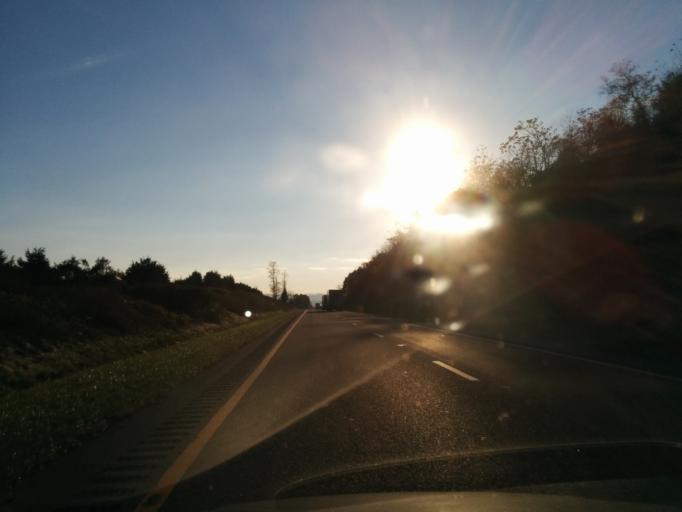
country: US
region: Virginia
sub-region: Rockbridge County
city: East Lexington
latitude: 37.8634
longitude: -79.3404
